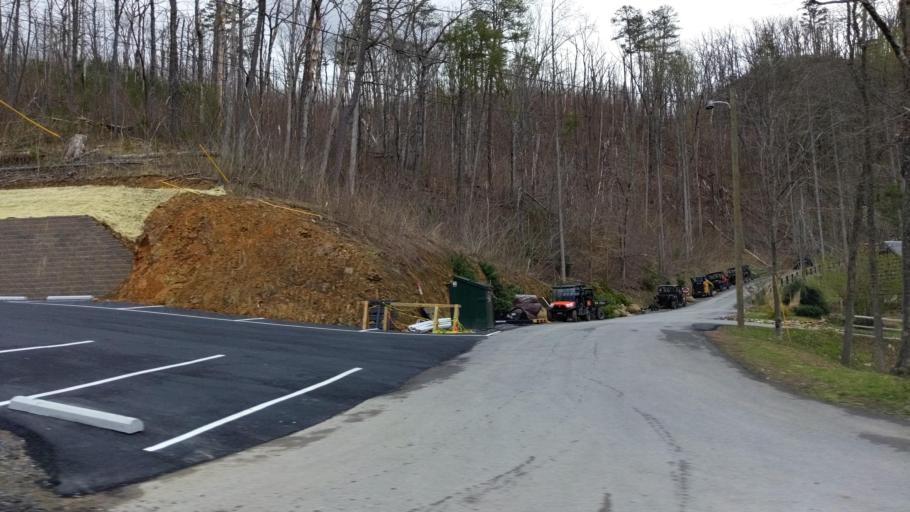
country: US
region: Tennessee
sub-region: Sevier County
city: Gatlinburg
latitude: 35.7131
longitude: -83.5077
